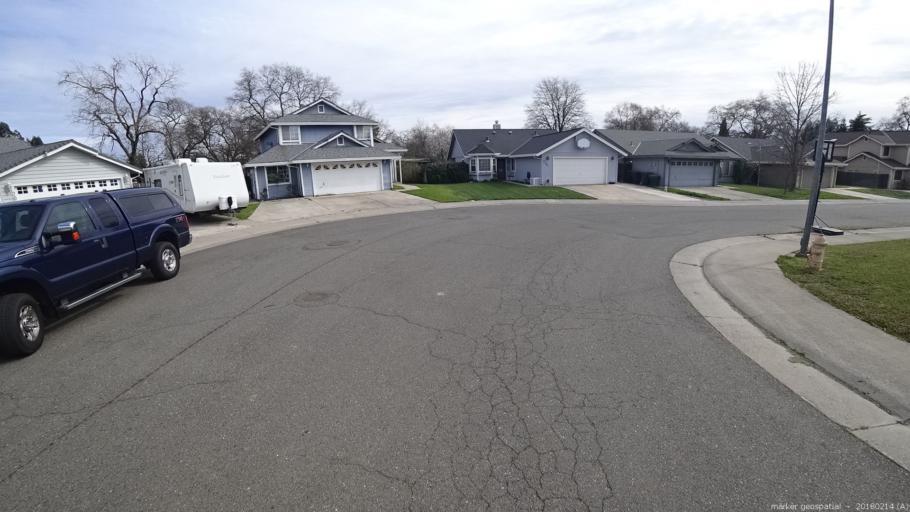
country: US
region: California
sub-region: Sacramento County
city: Rio Linda
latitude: 38.6961
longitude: -121.4402
